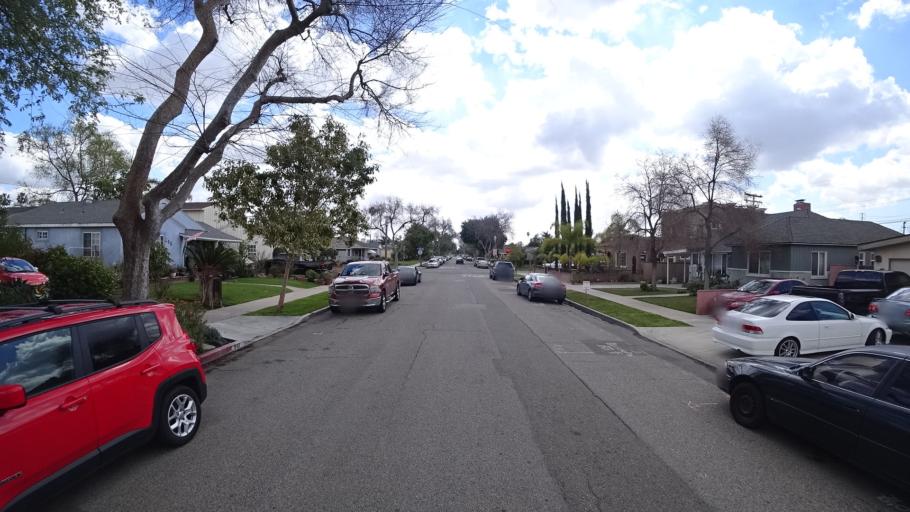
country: US
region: California
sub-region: Orange County
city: Anaheim
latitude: 33.8459
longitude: -117.9214
